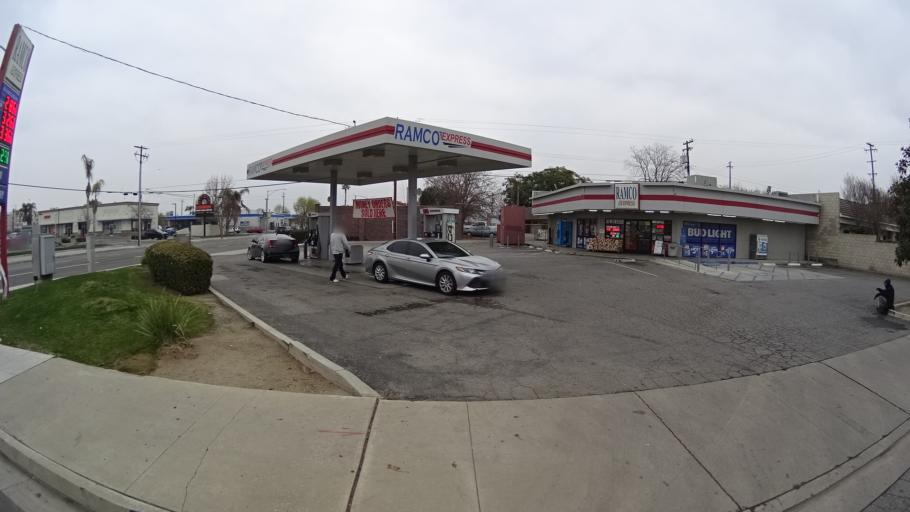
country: US
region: California
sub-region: Kern County
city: Bakersfield
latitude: 35.3798
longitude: -119.0234
